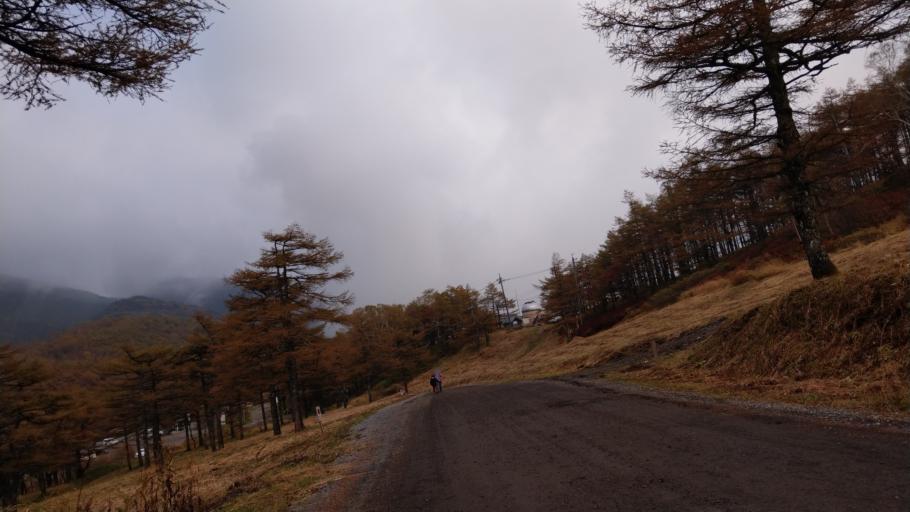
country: JP
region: Nagano
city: Komoro
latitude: 36.4055
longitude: 138.4675
